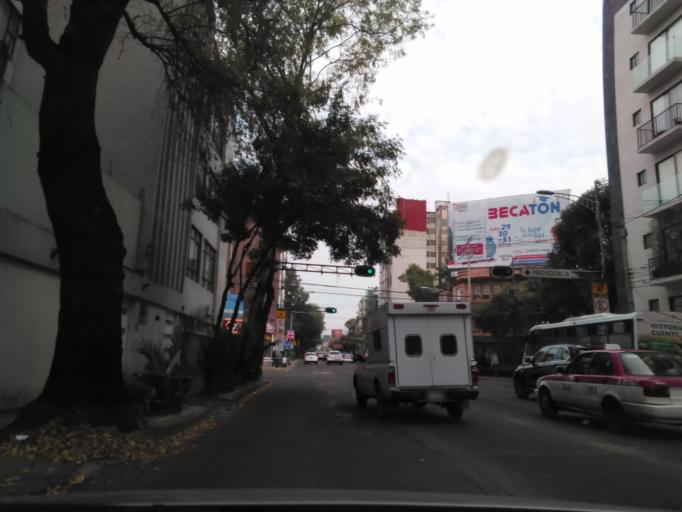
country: MX
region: Mexico City
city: Colonia del Valle
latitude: 19.3839
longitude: -99.1711
